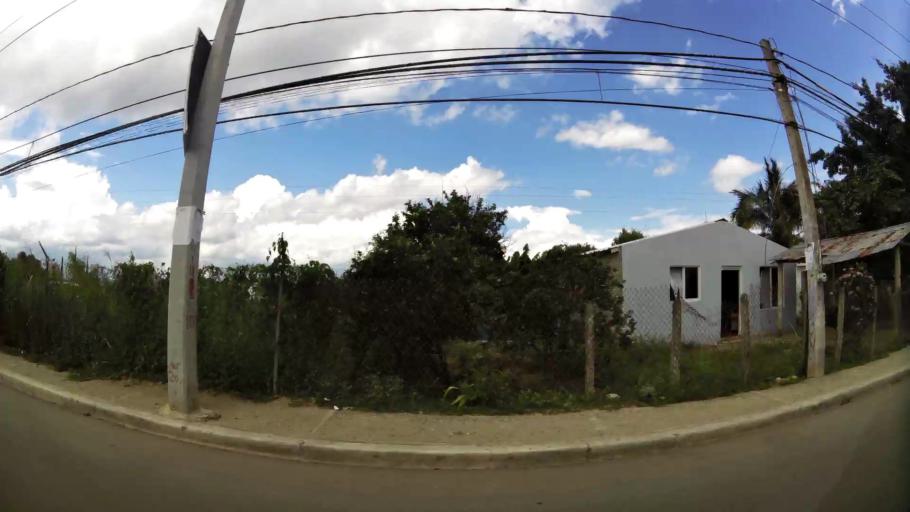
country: DO
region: Santiago
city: Licey al Medio
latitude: 19.3996
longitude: -70.6505
